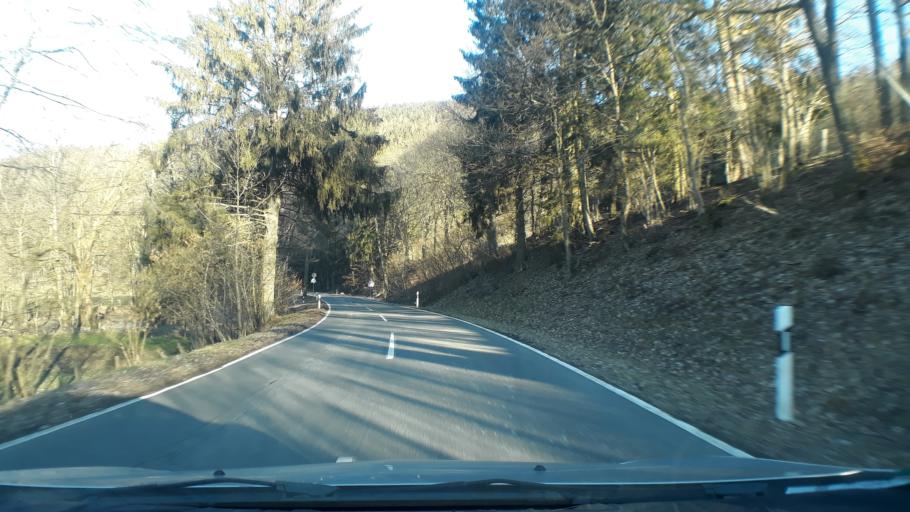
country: DE
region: North Rhine-Westphalia
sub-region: Regierungsbezirk Koln
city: Simmerath
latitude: 50.5692
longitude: 6.3394
